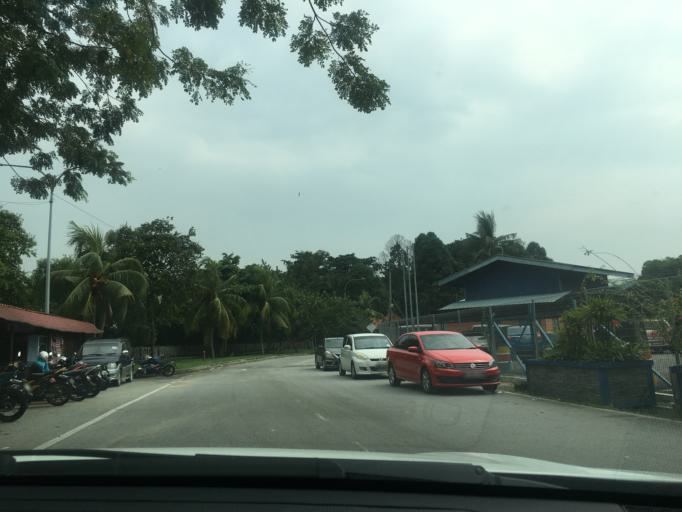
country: MY
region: Selangor
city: Klang
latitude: 3.0490
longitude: 101.4405
